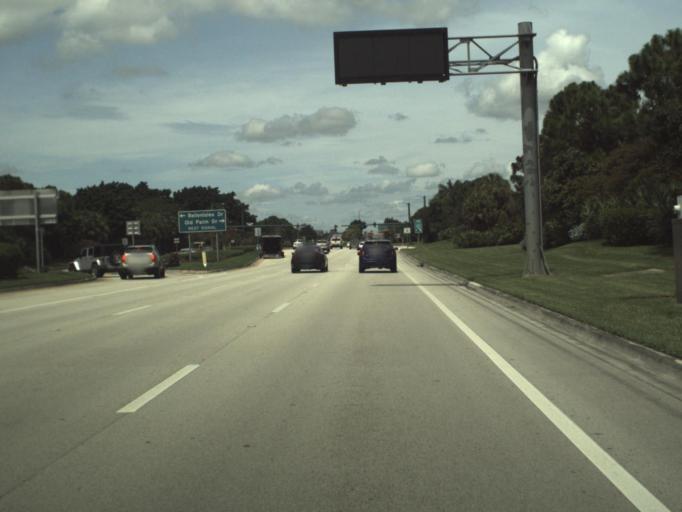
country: US
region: Florida
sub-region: Palm Beach County
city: Palm Beach Gardens
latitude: 26.8389
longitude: -80.1231
